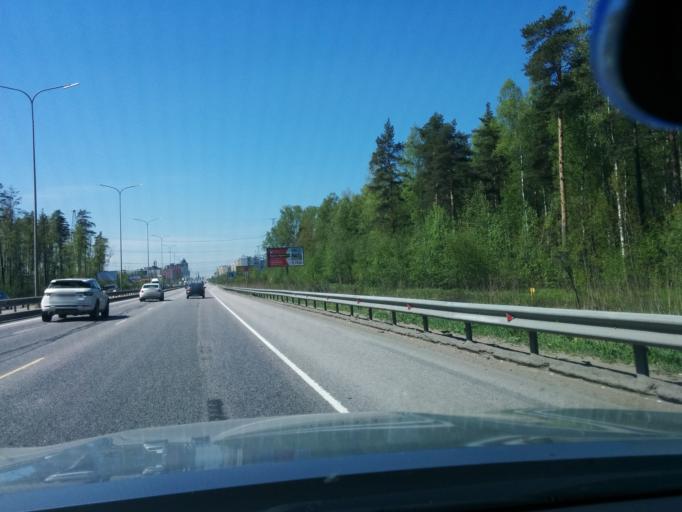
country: RU
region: St.-Petersburg
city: Krasnogvargeisky
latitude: 59.9459
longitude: 30.5278
